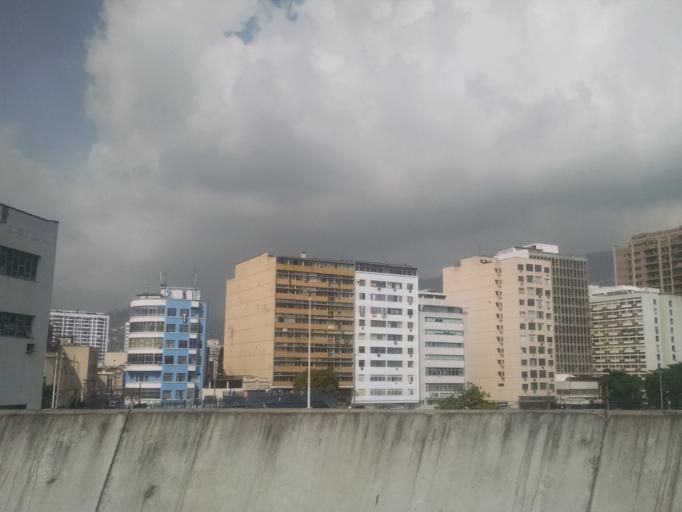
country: BR
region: Rio de Janeiro
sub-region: Rio De Janeiro
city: Rio de Janeiro
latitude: -22.9101
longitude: -43.2142
